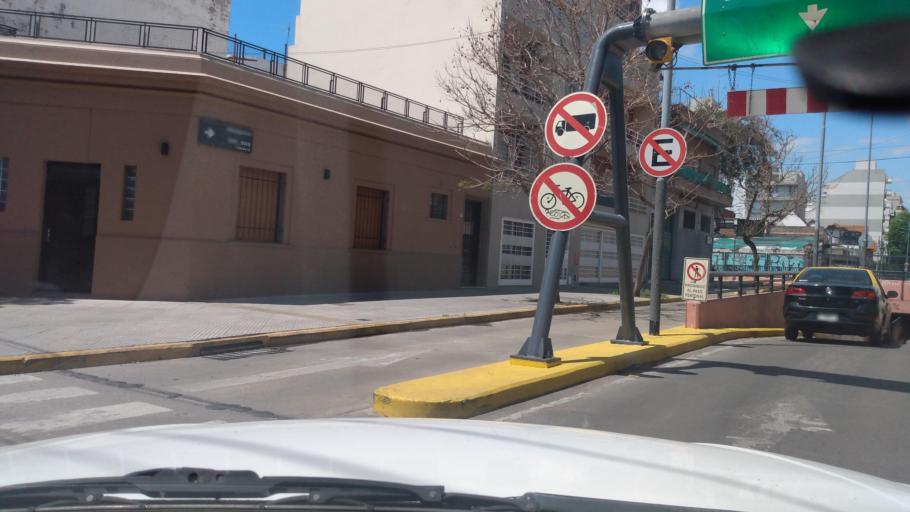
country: AR
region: Buenos Aires
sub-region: Partido de General San Martin
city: General San Martin
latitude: -34.5762
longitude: -58.4916
